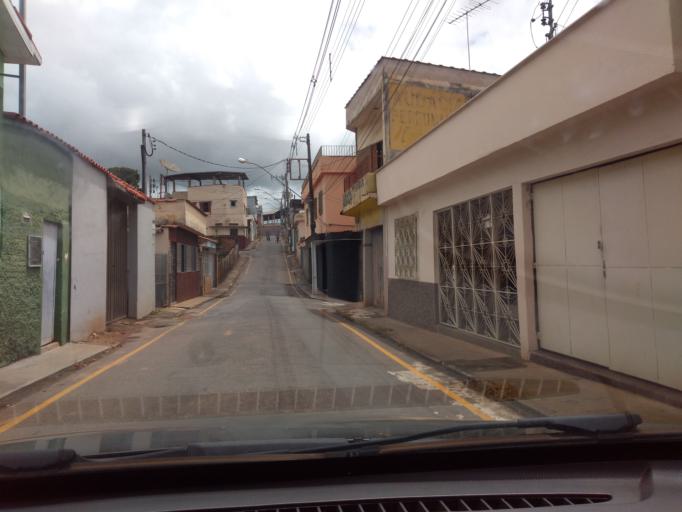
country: BR
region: Minas Gerais
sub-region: Tres Coracoes
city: Tres Coracoes
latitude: -21.6927
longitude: -45.2539
